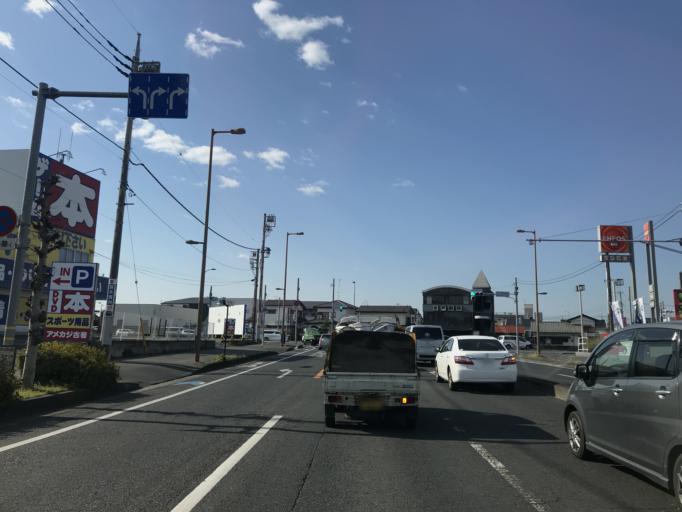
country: JP
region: Ibaraki
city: Mito-shi
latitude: 36.3464
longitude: 140.4718
